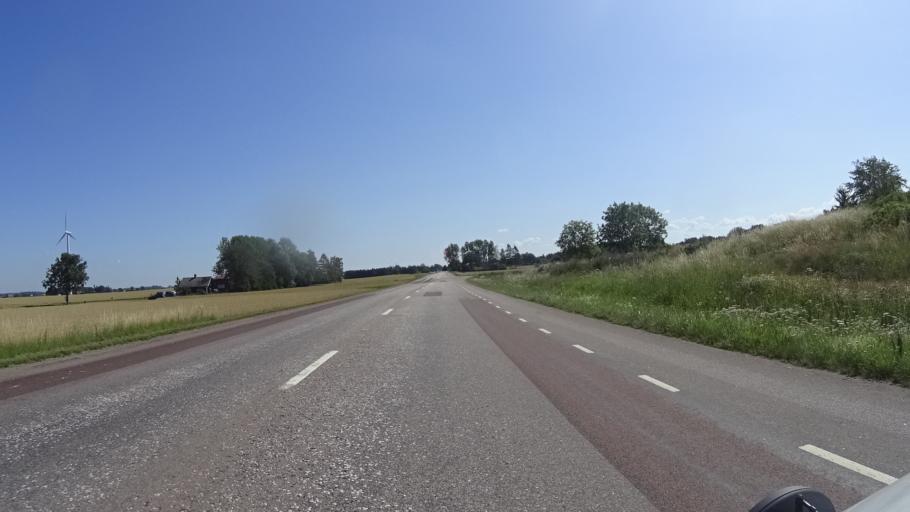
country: SE
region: OEstergoetland
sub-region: Vadstena Kommun
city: Herrestad
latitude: 58.3098
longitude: 14.8798
